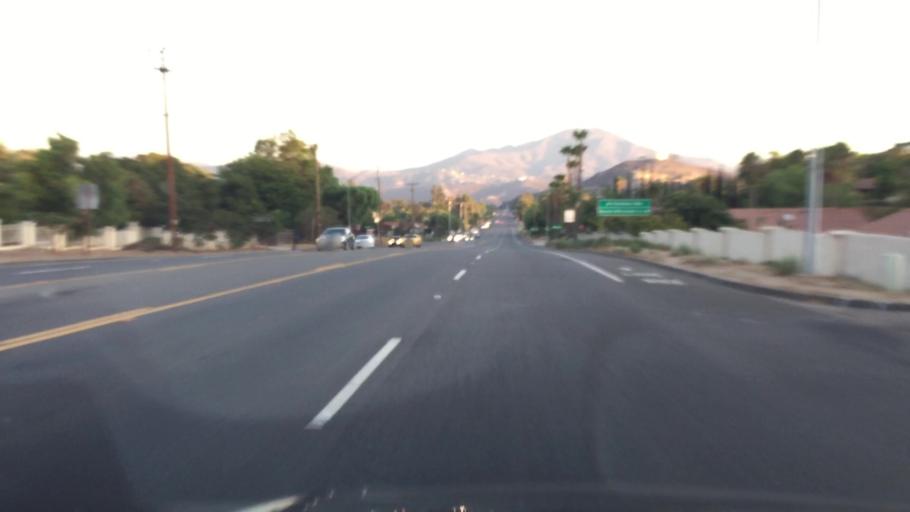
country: US
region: California
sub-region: San Diego County
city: Rancho San Diego
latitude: 32.7756
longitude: -116.9280
